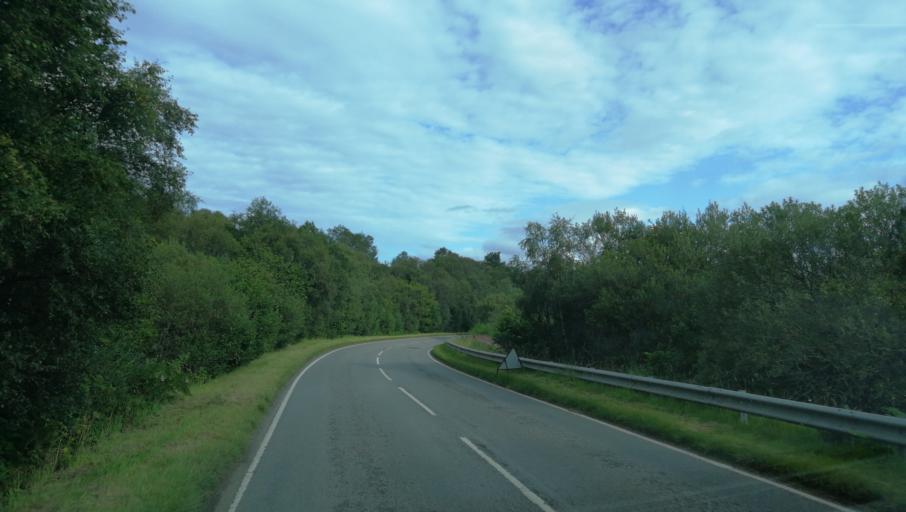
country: GB
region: Scotland
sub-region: Highland
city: Alness
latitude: 58.0320
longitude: -4.4180
